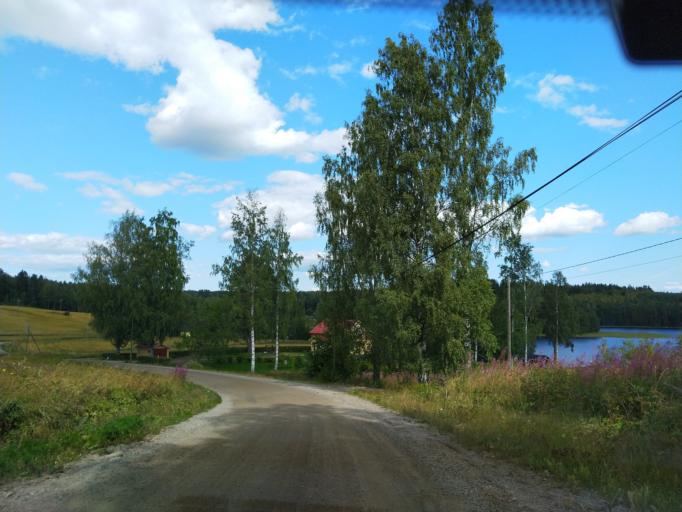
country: FI
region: Pirkanmaa
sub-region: Ylae-Pirkanmaa
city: Ruovesi
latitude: 61.9595
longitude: 24.0343
